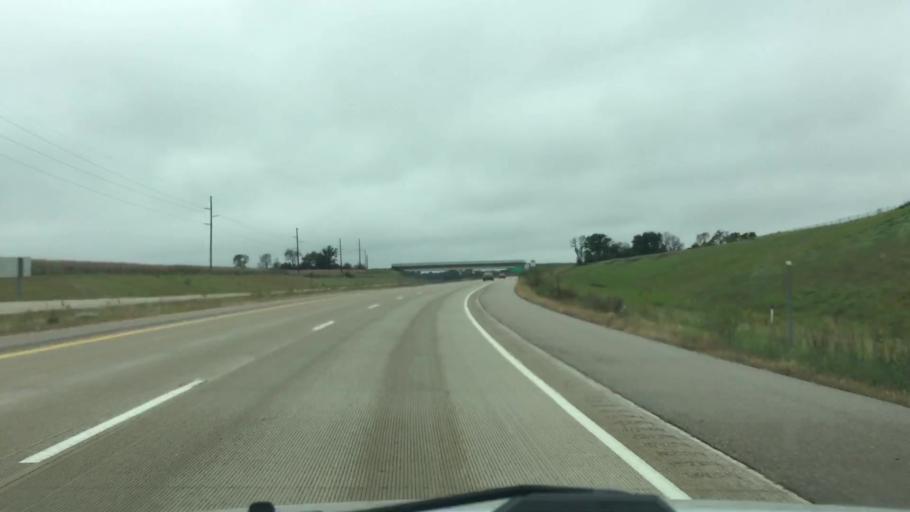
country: US
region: Wisconsin
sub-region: Rock County
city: Milton
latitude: 42.7624
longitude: -88.9303
